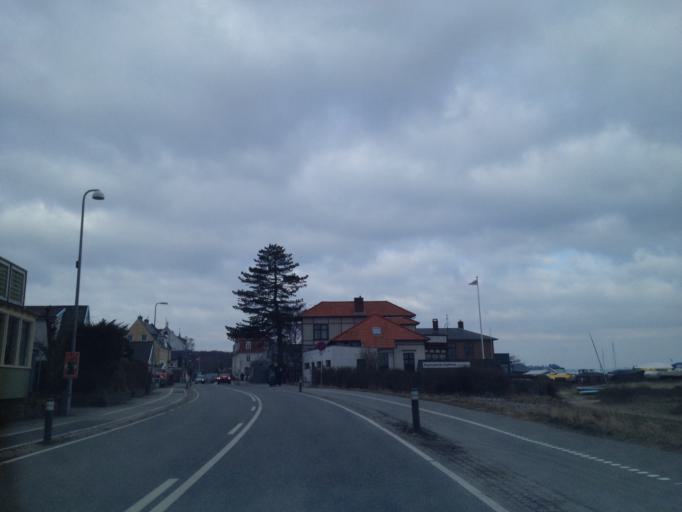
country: DK
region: Capital Region
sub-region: Helsingor Kommune
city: Espergaerde
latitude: 55.9911
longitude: 12.5600
